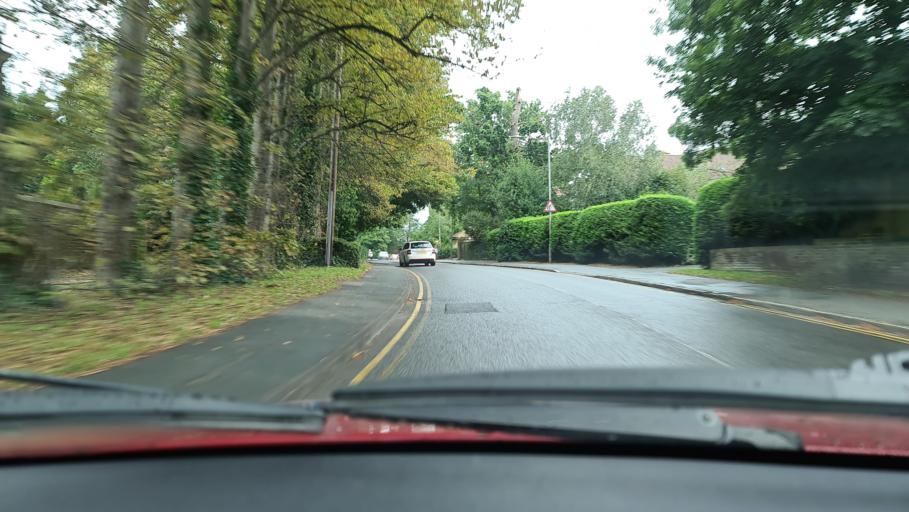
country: GB
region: England
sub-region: Buckinghamshire
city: Beaconsfield
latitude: 51.6089
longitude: -0.6443
